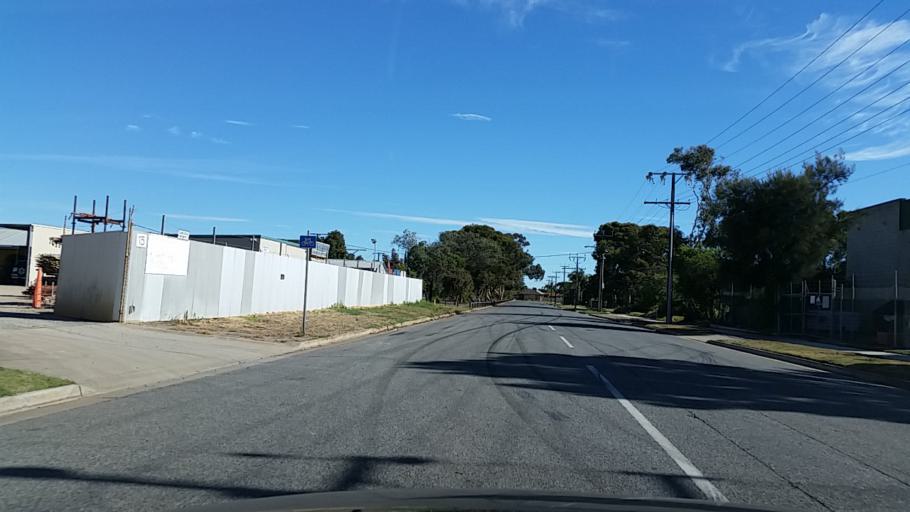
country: AU
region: South Australia
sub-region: Port Adelaide Enfield
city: Cheltenham
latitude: -34.8655
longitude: 138.5073
